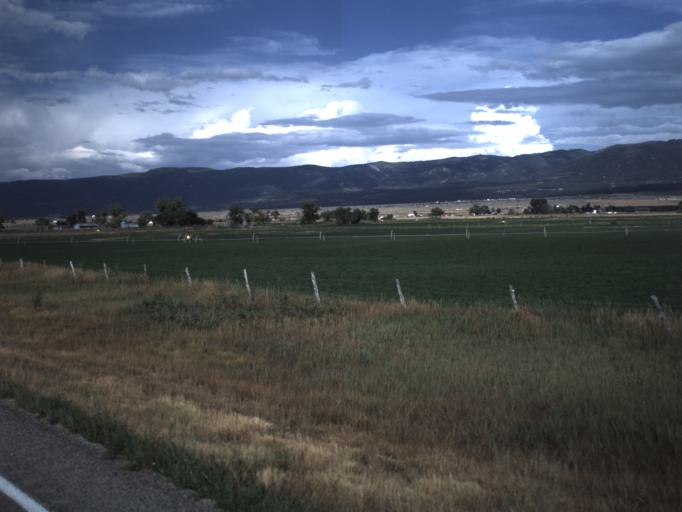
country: US
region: Utah
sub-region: Sanpete County
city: Mount Pleasant
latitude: 39.4975
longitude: -111.5074
